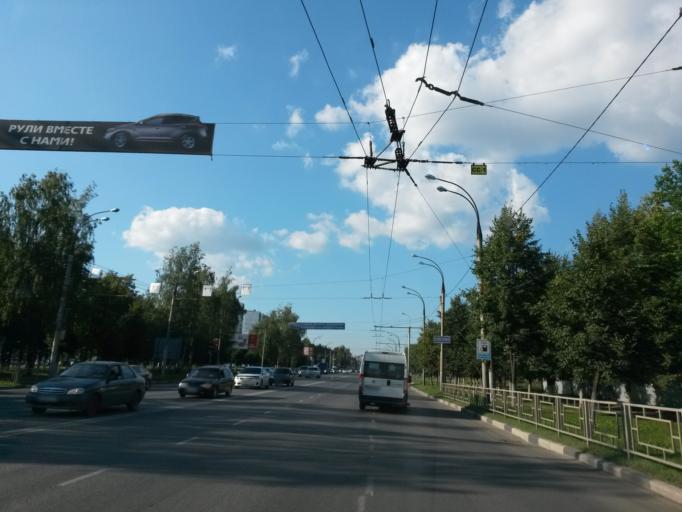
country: RU
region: Ivanovo
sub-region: Gorod Ivanovo
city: Ivanovo
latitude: 56.9588
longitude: 40.9742
